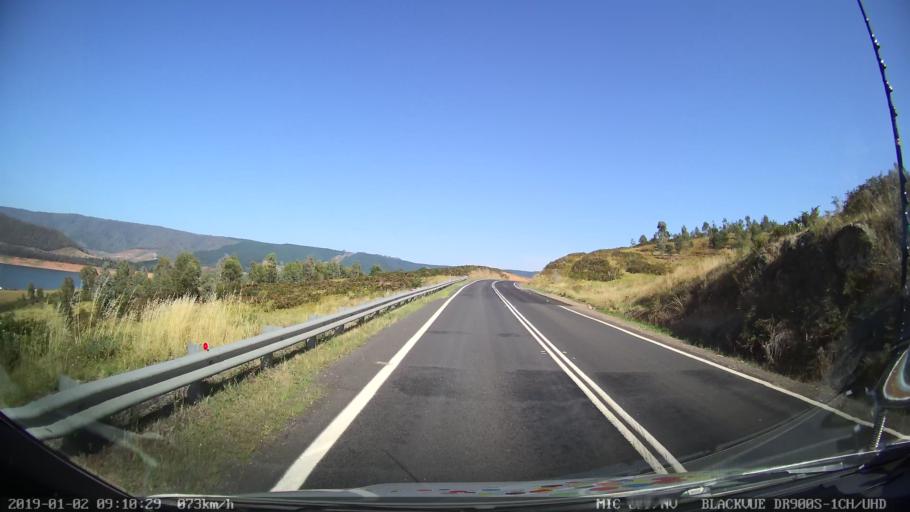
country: AU
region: New South Wales
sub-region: Tumut Shire
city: Tumut
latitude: -35.5211
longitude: 148.2699
